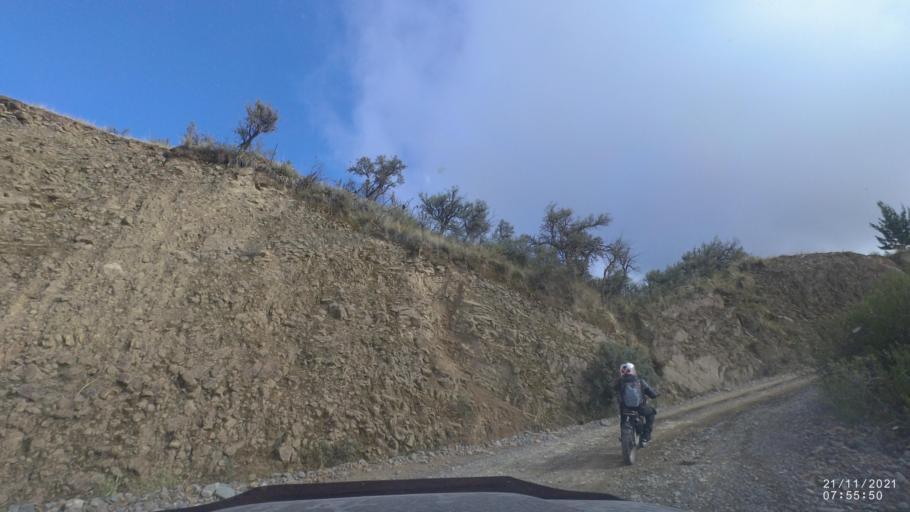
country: BO
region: Cochabamba
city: Cochabamba
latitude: -17.2984
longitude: -66.2182
